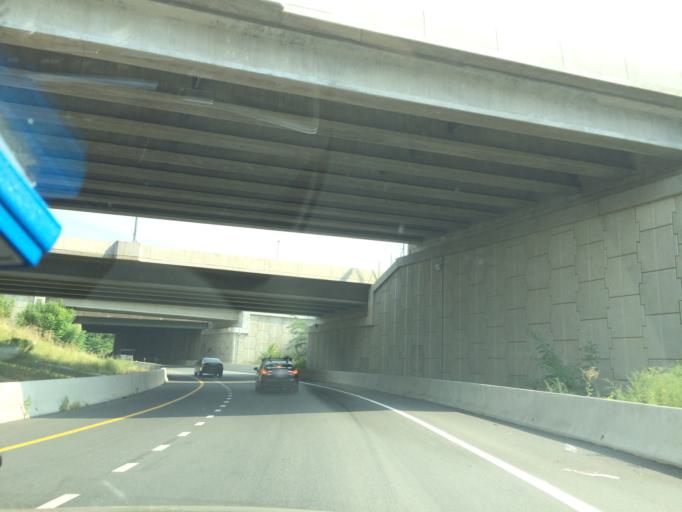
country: US
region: Virginia
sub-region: Fairfax County
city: Pimmit Hills
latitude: 38.9298
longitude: -77.2124
